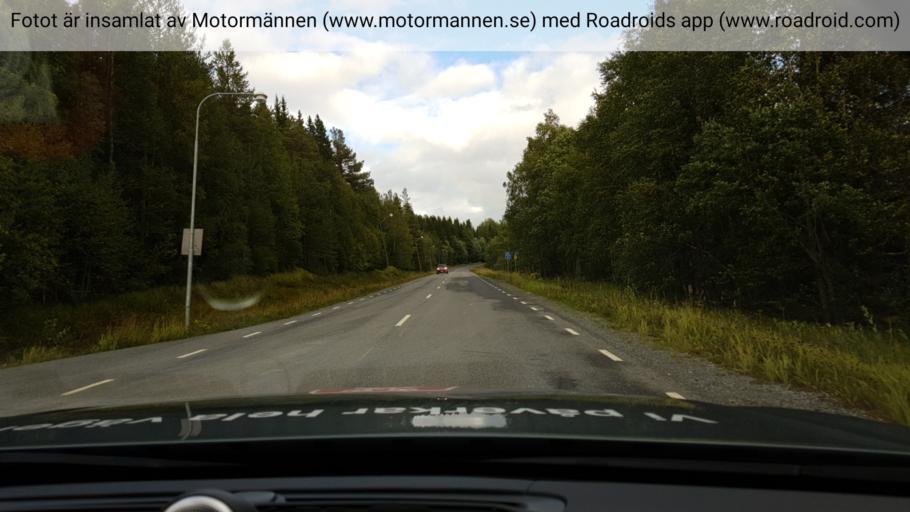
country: SE
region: Jaemtland
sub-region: Krokoms Kommun
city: Krokom
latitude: 63.6767
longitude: 14.5784
